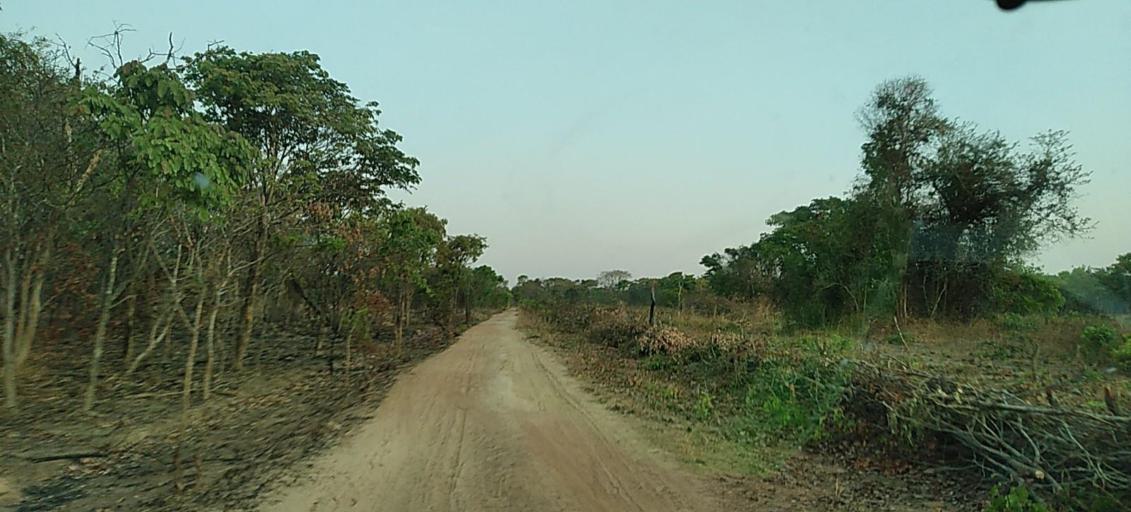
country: ZM
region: North-Western
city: Kalengwa
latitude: -13.1108
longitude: 25.1661
